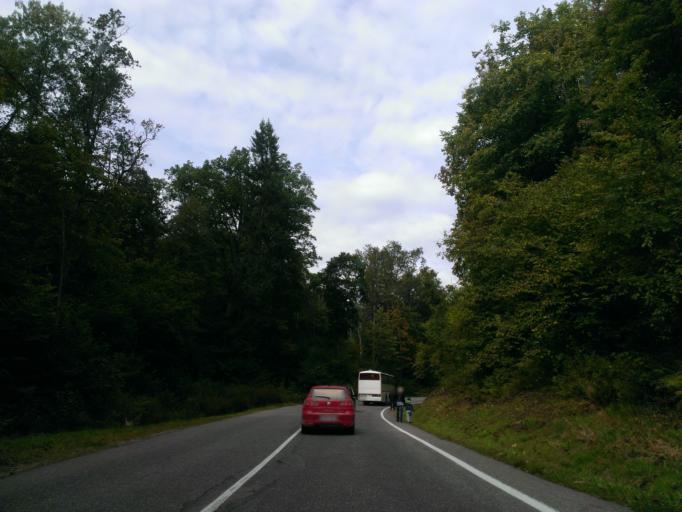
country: LV
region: Sigulda
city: Sigulda
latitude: 57.1827
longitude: 24.8481
